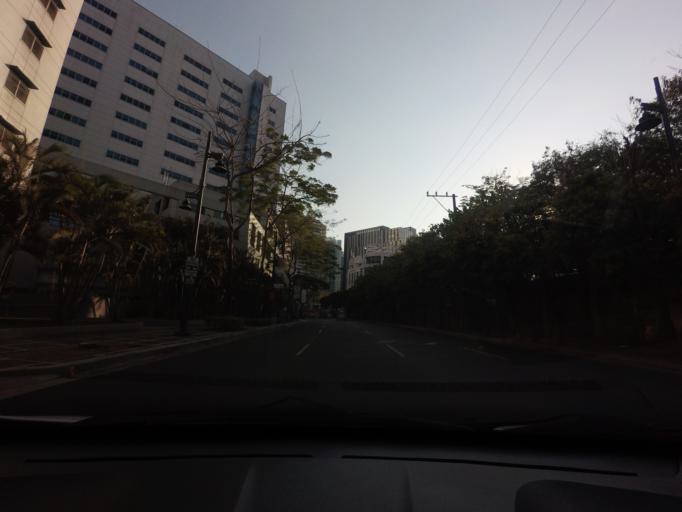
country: PH
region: Metro Manila
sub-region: Makati City
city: Makati City
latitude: 14.5557
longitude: 121.0483
